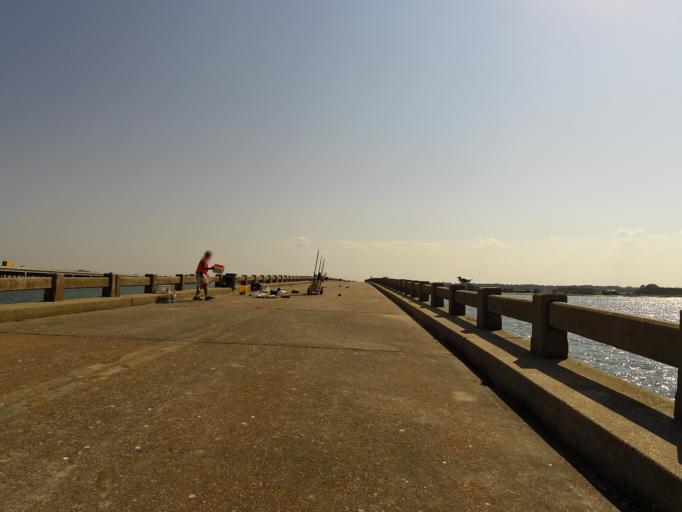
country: US
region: Florida
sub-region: Nassau County
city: Fernandina Beach
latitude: 30.5195
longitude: -81.4505
